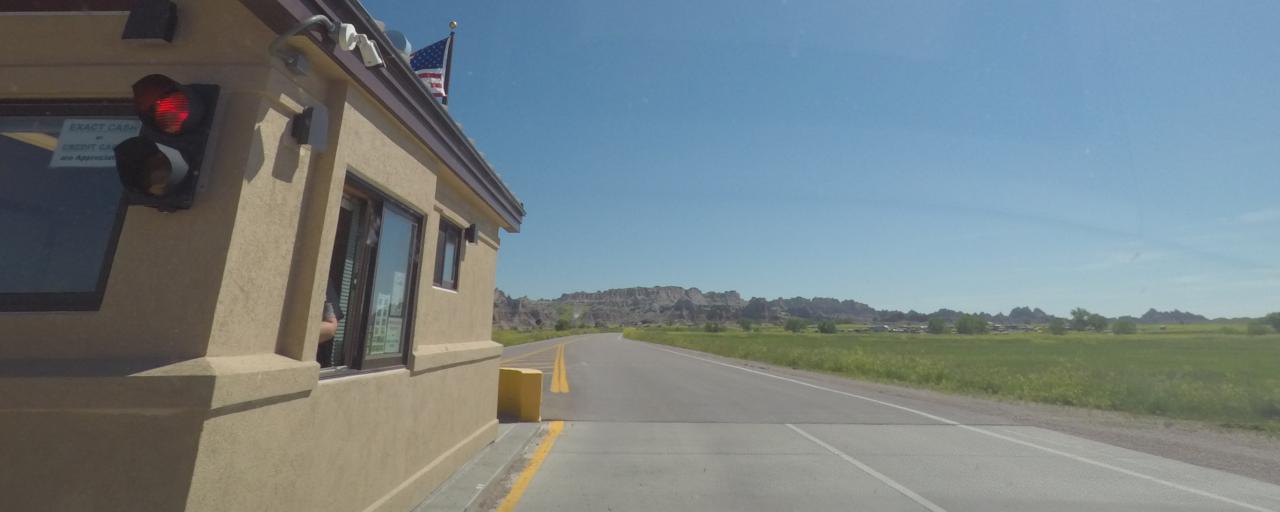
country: US
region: South Dakota
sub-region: Haakon County
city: Philip
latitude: 43.7425
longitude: -101.9563
